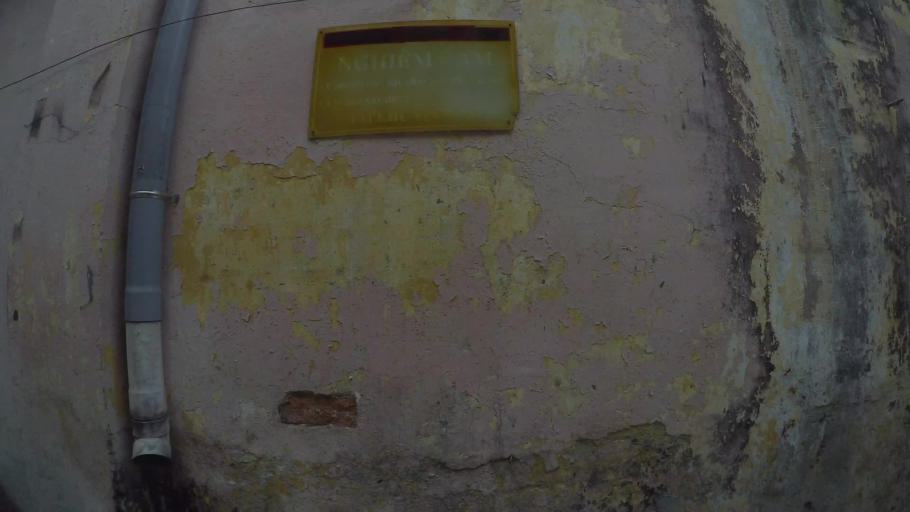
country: VN
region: Da Nang
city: Da Nang
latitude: 16.0840
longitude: 108.2205
